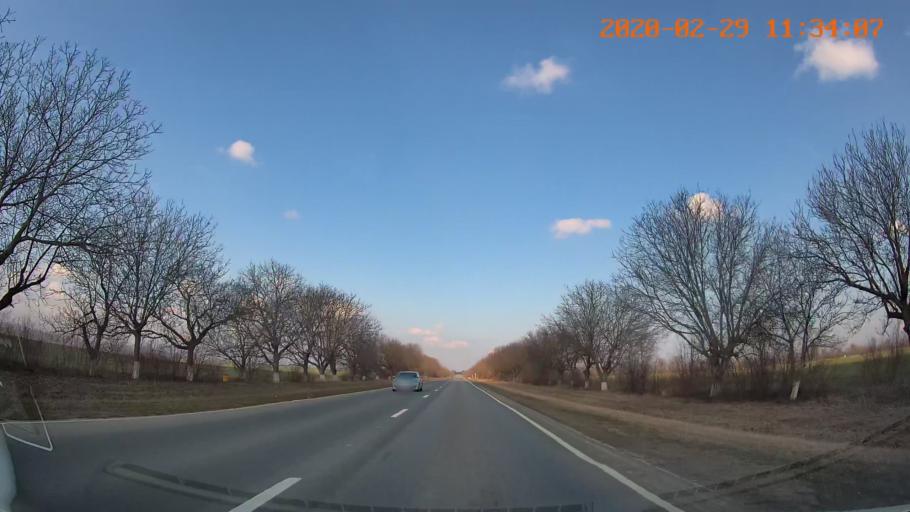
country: MD
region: Rezina
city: Saharna
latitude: 47.5610
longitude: 29.0774
